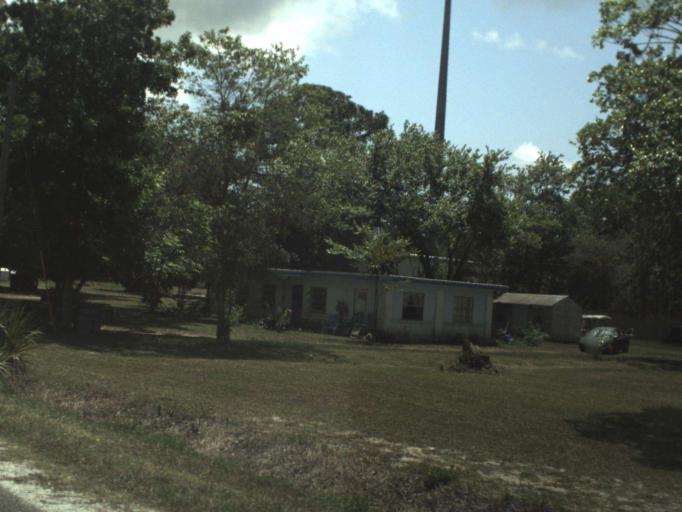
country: US
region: Florida
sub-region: Volusia County
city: Oak Hill
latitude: 28.8602
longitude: -80.8514
